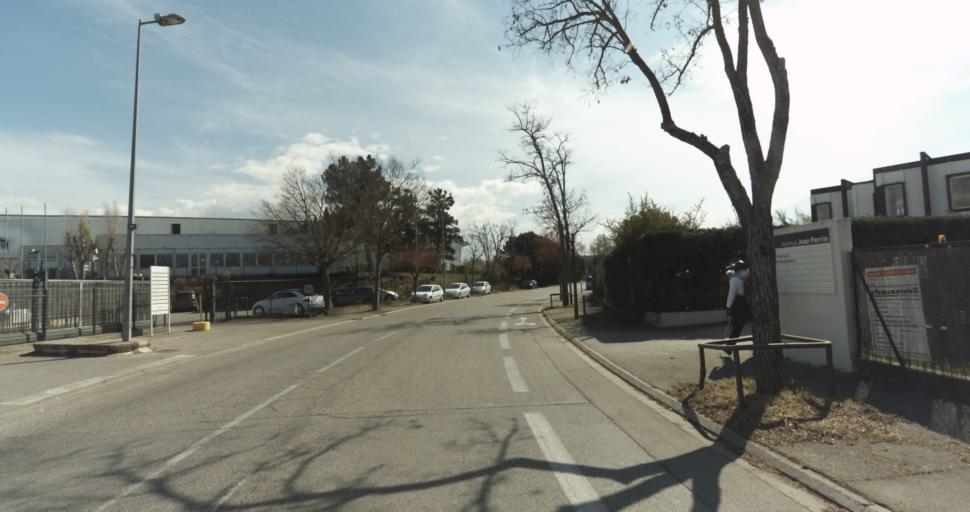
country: FR
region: Provence-Alpes-Cote d'Azur
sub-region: Departement des Bouches-du-Rhone
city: Cabries
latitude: 43.4871
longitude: 5.3724
